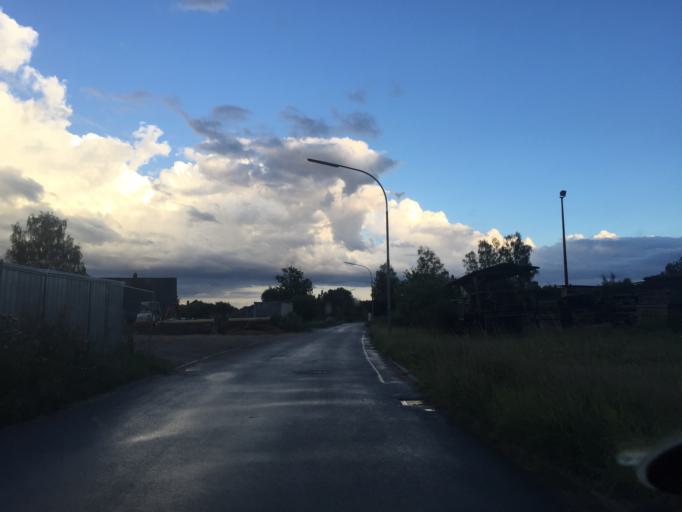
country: DE
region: Bavaria
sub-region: Upper Palatinate
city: Pressath
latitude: 49.7600
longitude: 11.9419
